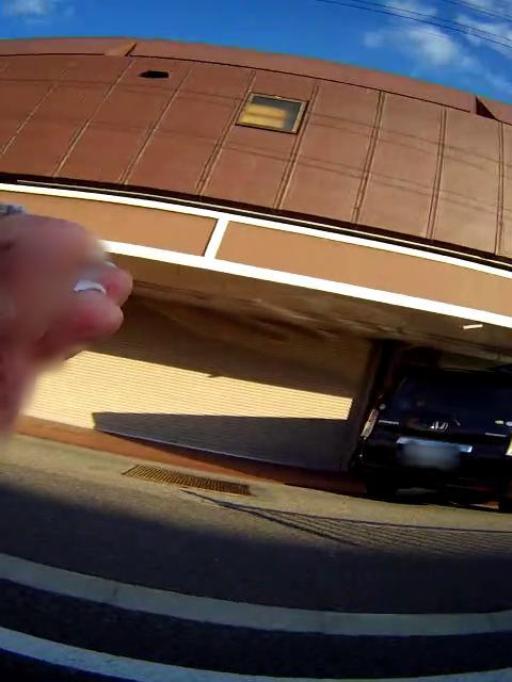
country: JP
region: Hyogo
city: Itami
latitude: 34.7601
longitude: 135.4119
